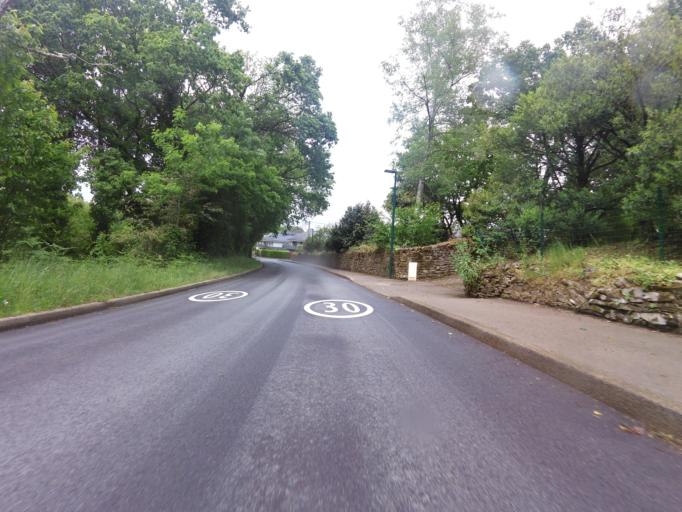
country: FR
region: Brittany
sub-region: Departement du Morbihan
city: Baden
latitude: 47.6205
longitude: -2.9217
